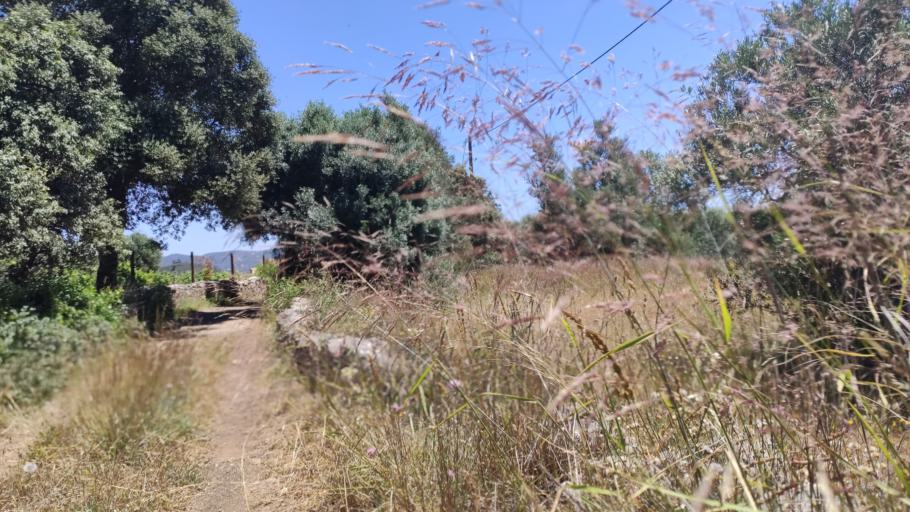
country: PT
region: Faro
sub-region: Sao Bras de Alportel
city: Sao Bras de Alportel
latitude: 37.1709
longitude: -7.9038
